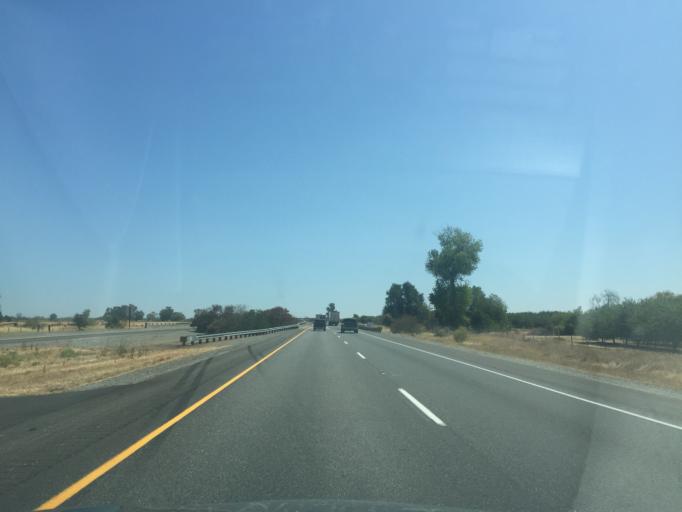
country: US
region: California
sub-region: Tehama County
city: Gerber
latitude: 40.0112
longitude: -122.2078
